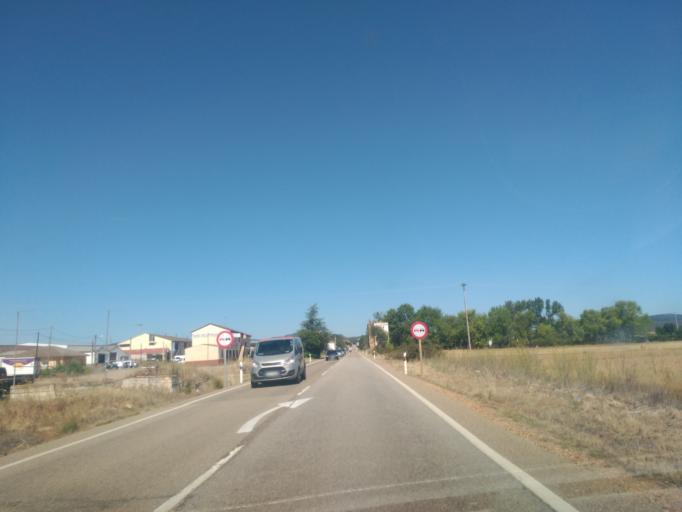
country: ES
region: Castille and Leon
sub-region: Provincia de Zamora
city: Tabara
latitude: 41.8201
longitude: -5.9487
